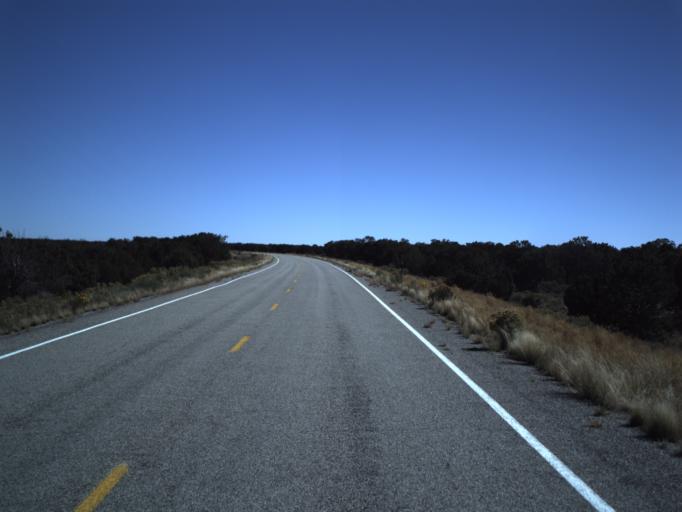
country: US
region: Utah
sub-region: San Juan County
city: Blanding
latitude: 37.5407
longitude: -109.9692
